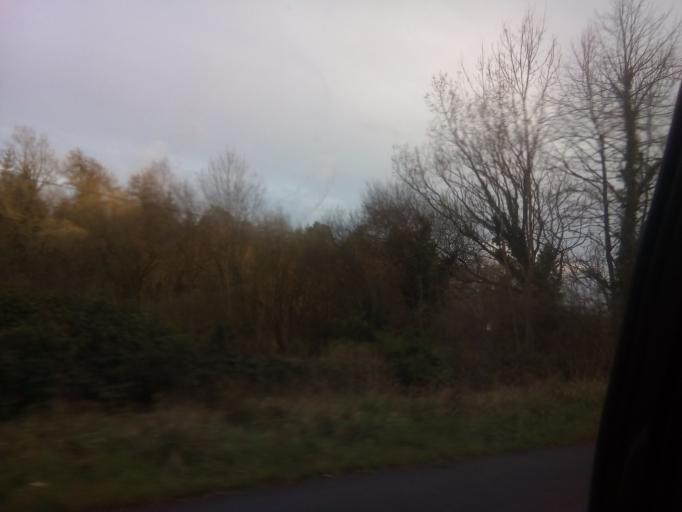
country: IE
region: Leinster
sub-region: Laois
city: Abbeyleix
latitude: 52.8895
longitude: -7.3636
